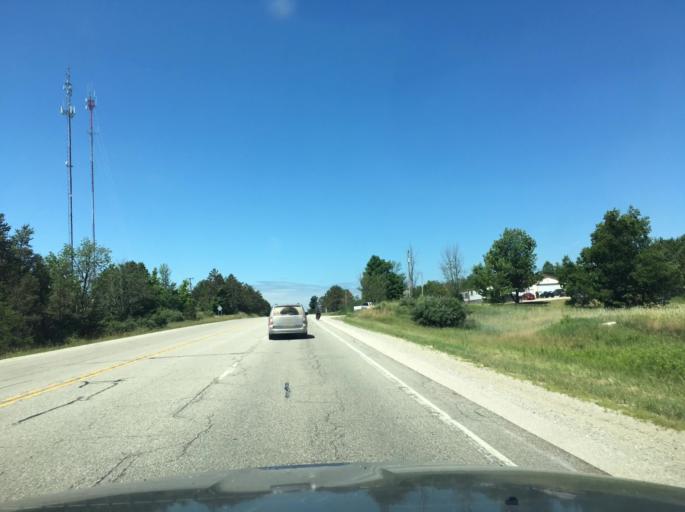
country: US
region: Michigan
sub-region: Osceola County
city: Reed City
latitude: 43.8878
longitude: -85.5911
